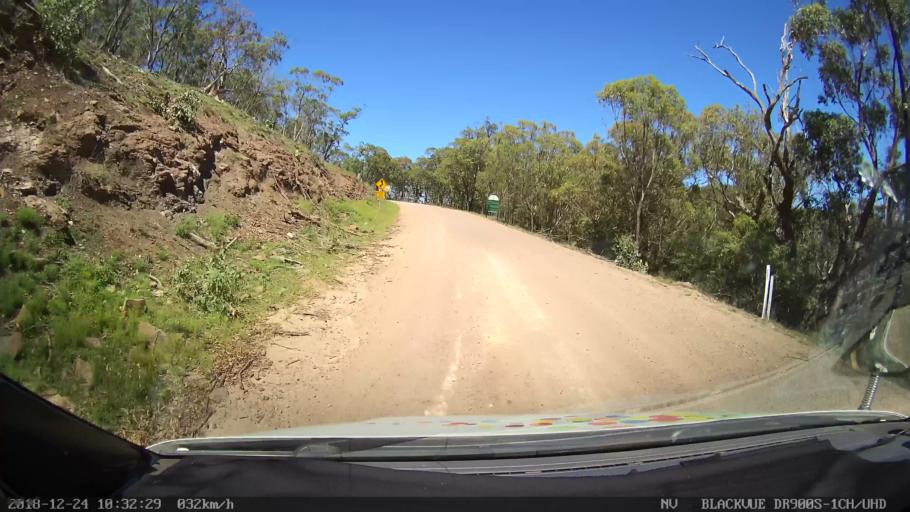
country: AU
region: New South Wales
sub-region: Upper Hunter Shire
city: Merriwa
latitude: -31.8414
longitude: 150.5158
